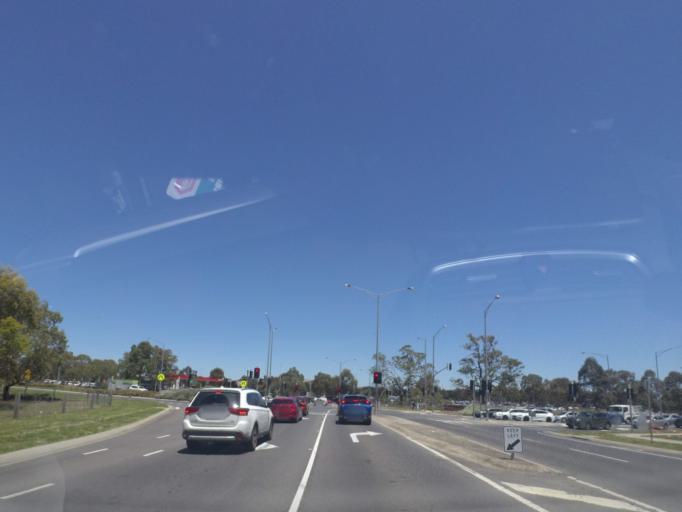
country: AU
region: Victoria
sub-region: Whittlesea
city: Mill Park
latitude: -37.6503
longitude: 145.0764
